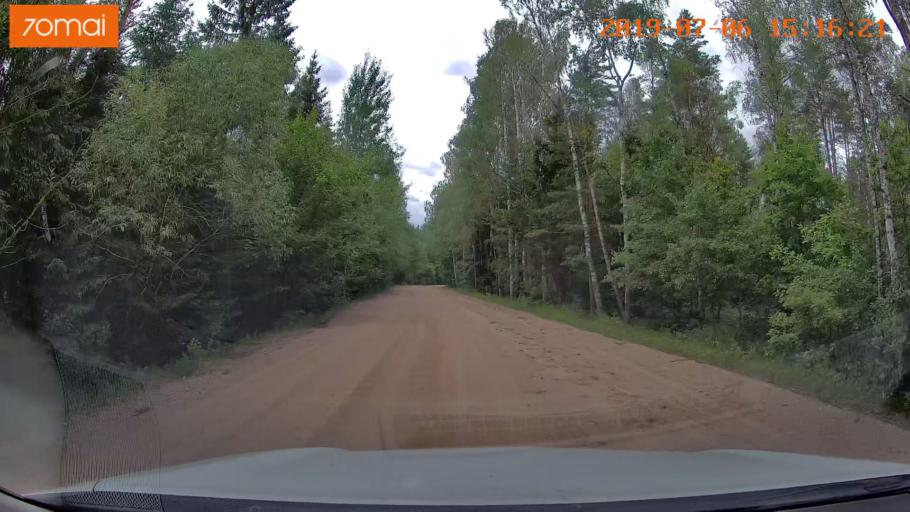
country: BY
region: Minsk
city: Ivyanyets
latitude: 53.9805
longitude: 26.6796
